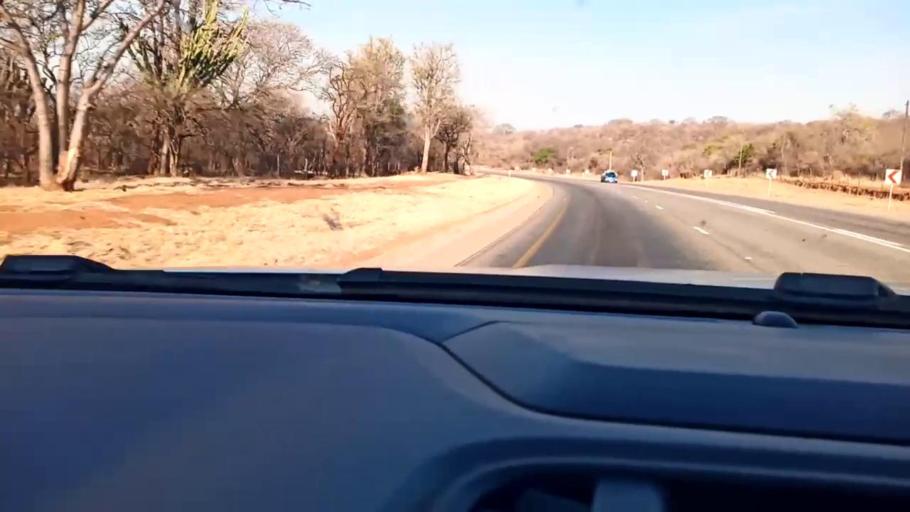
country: ZA
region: Limpopo
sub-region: Mopani District Municipality
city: Duiwelskloof
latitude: -23.6360
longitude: 30.1418
